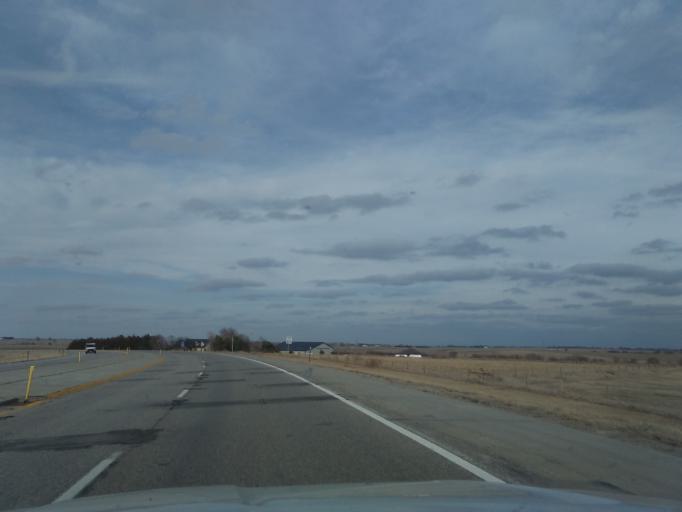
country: US
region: Nebraska
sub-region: Lancaster County
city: Hickman
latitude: 40.4682
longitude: -96.7068
